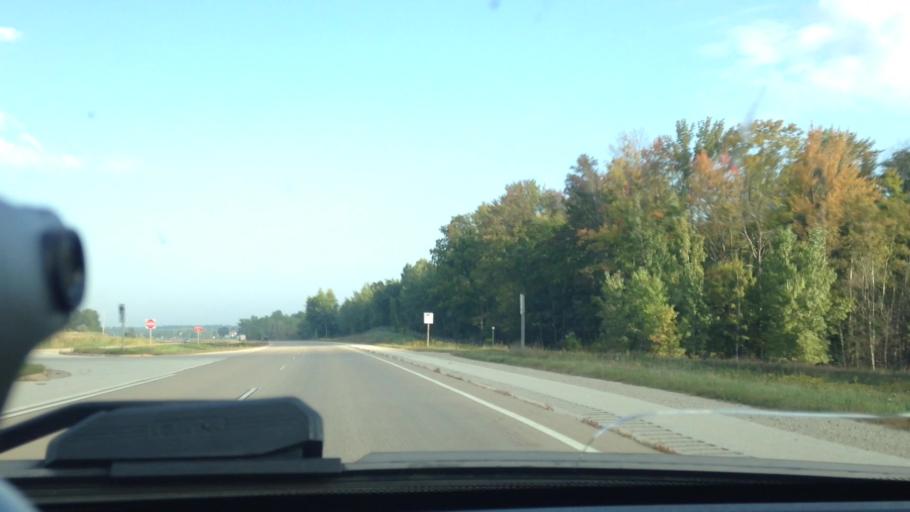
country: US
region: Wisconsin
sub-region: Oconto County
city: Oconto Falls
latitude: 44.9721
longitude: -88.0375
